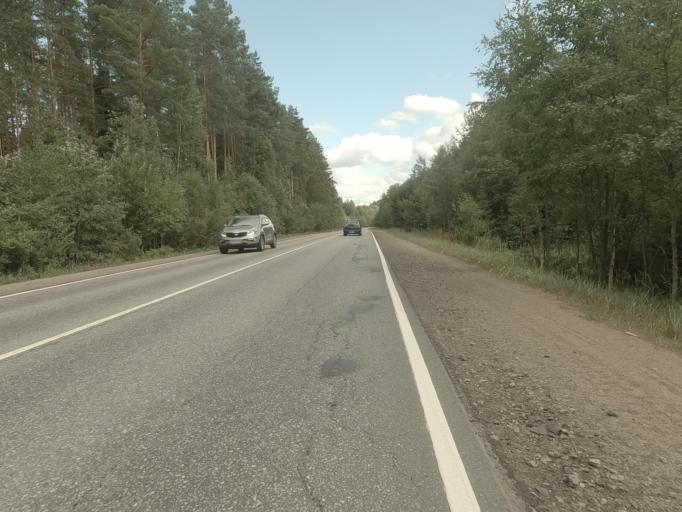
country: RU
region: Leningrad
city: Shcheglovo
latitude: 60.0094
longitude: 30.8581
